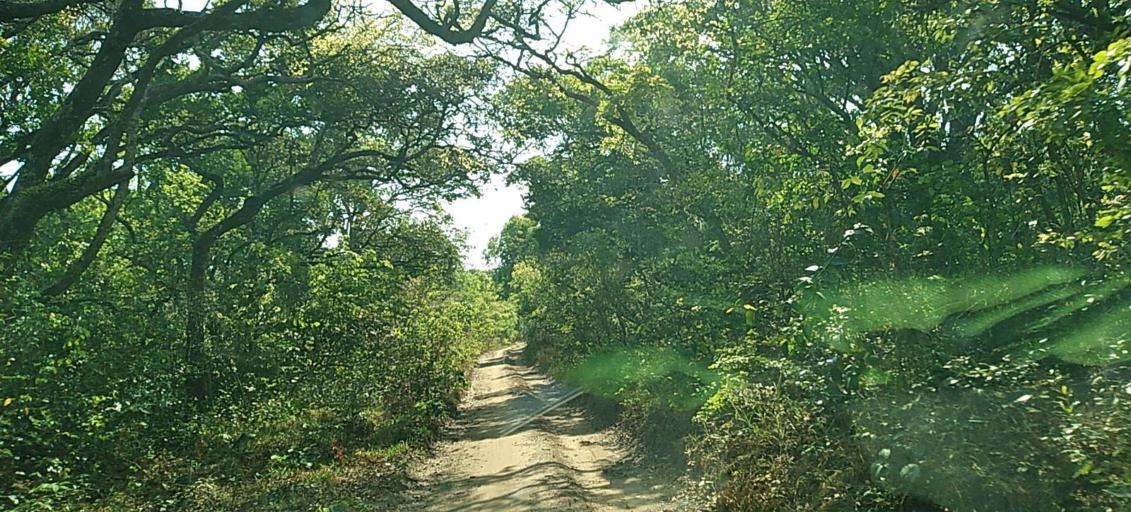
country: ZM
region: North-Western
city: Mwinilunga
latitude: -11.3016
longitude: 24.8431
